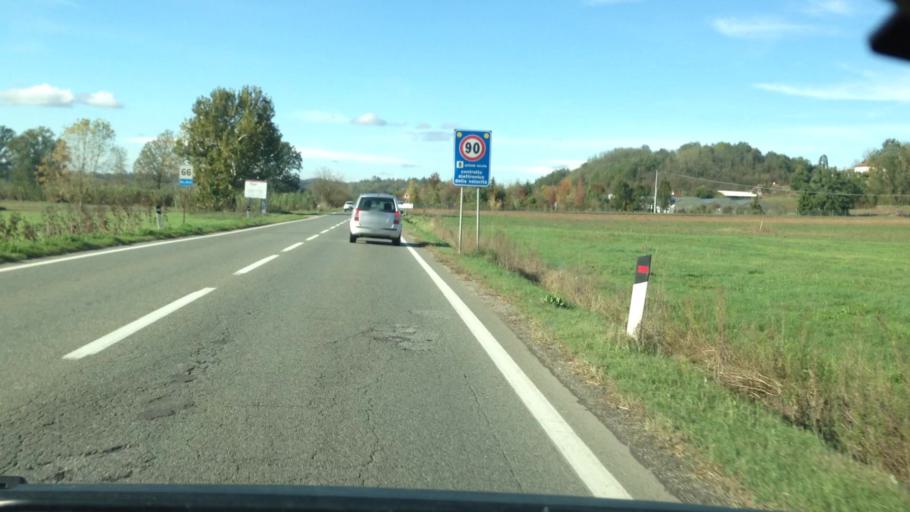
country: IT
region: Piedmont
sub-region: Provincia di Asti
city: Castello di Annone
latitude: 44.8957
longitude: 8.2977
